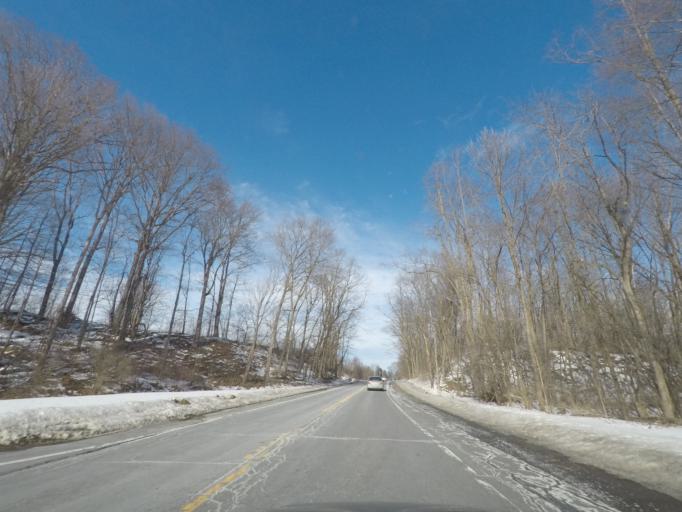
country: US
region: New York
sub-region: Albany County
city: Altamont
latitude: 42.7234
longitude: -73.9920
